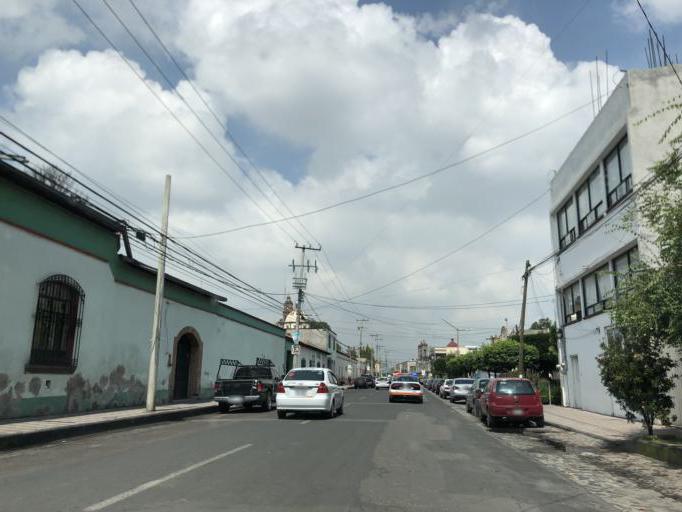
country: MX
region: Morelos
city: Lerma de Villada
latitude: 19.2861
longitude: -99.5083
